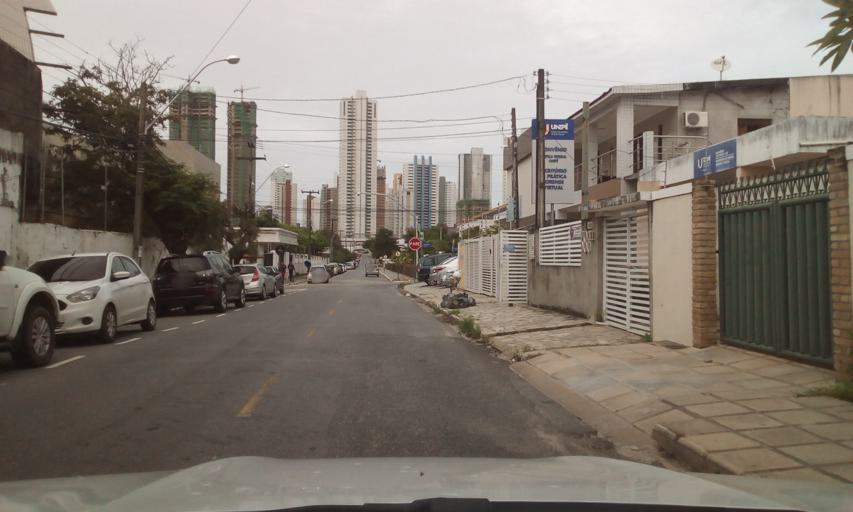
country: BR
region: Paraiba
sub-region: Joao Pessoa
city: Joao Pessoa
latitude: -7.1156
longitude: -34.8462
